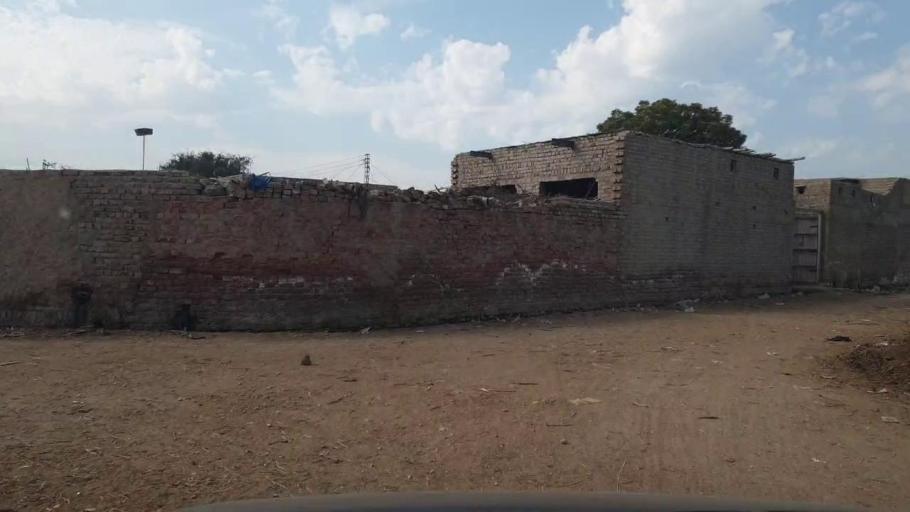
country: PK
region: Sindh
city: Sakrand
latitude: 26.0065
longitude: 68.4127
